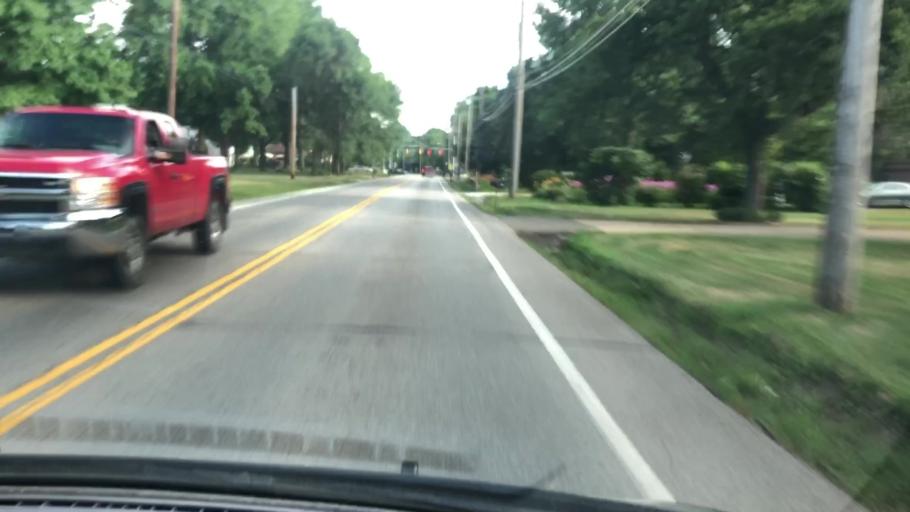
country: US
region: Ohio
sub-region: Summit County
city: Silver Lake
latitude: 41.1607
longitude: -81.4770
